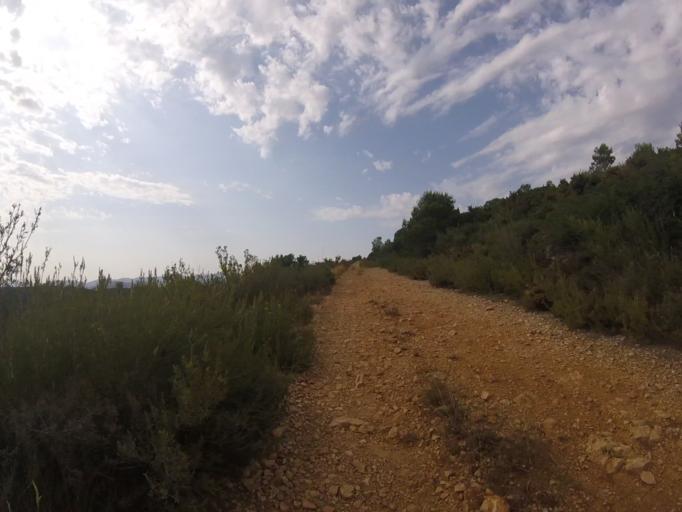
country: ES
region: Valencia
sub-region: Provincia de Castello
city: Alcala de Xivert
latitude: 40.3853
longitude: 0.2119
